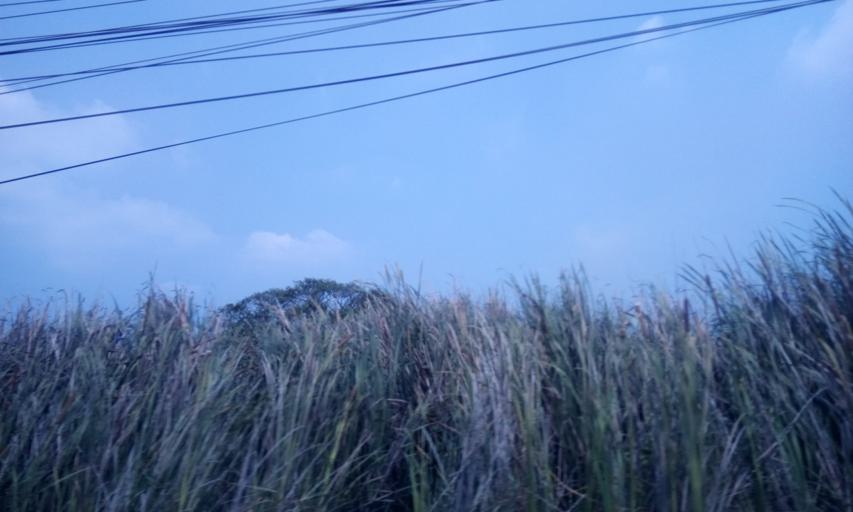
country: TH
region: Pathum Thani
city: Ban Lam Luk Ka
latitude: 13.9577
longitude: 100.8595
